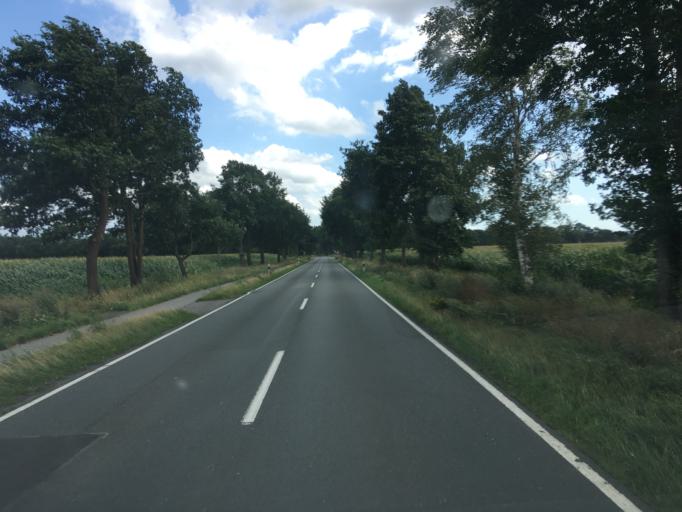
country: DE
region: Lower Saxony
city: Friesoythe
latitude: 53.0590
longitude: 7.8517
